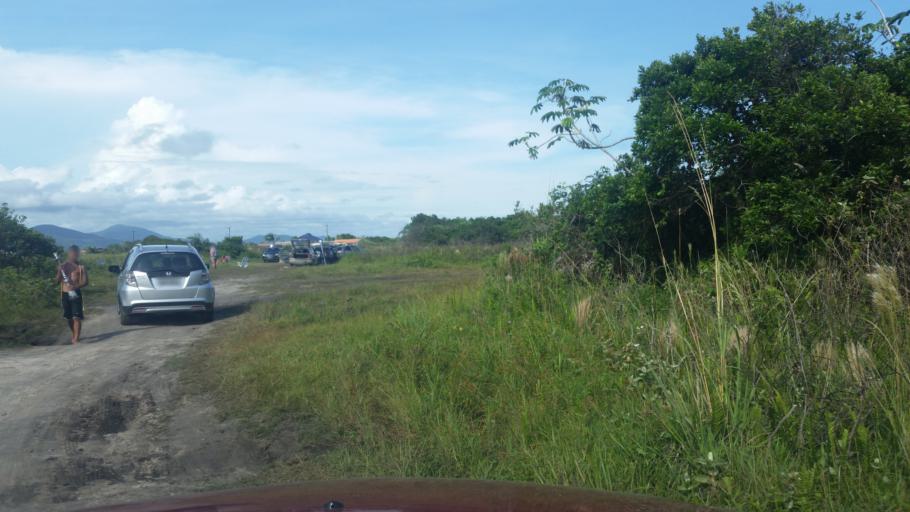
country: BR
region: Sao Paulo
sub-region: Iguape
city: Iguape
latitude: -24.7672
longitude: -47.5890
